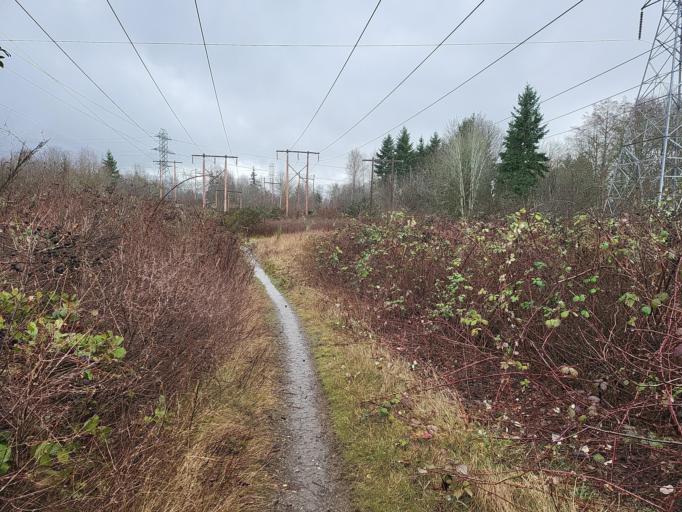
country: US
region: Washington
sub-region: King County
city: Renton
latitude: 47.4692
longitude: -122.1966
